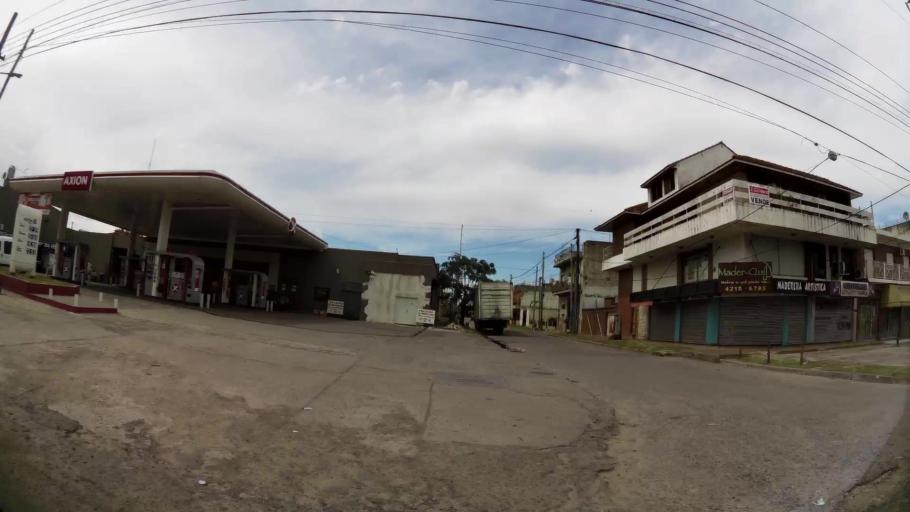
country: AR
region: Buenos Aires
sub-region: Partido de Quilmes
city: Quilmes
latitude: -34.7672
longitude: -58.2729
